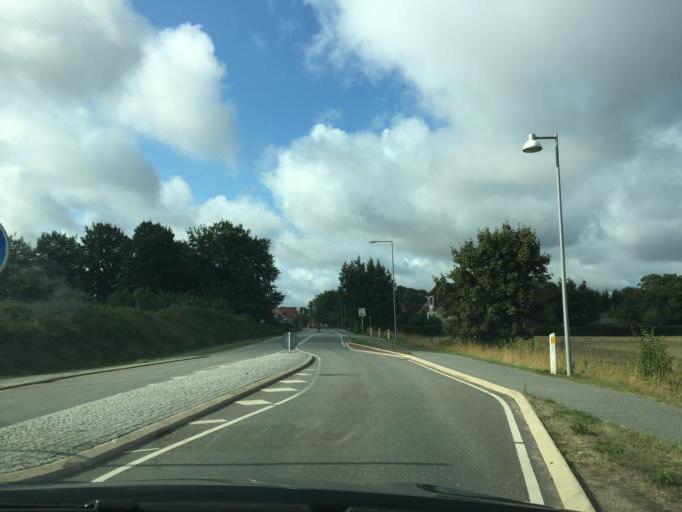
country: DK
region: South Denmark
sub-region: Odense Kommune
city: Hojby
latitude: 55.3083
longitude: 10.3976
